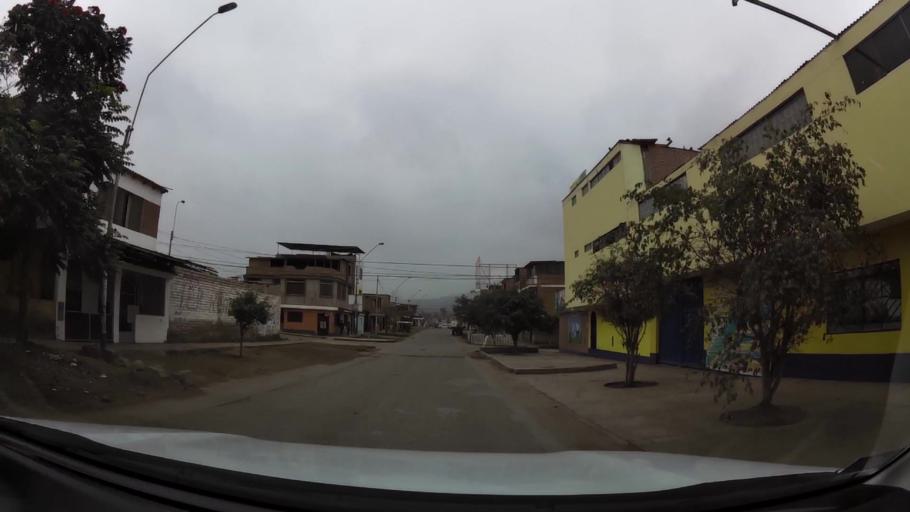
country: PE
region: Lima
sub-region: Lima
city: Cieneguilla
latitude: -12.2260
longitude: -76.9076
